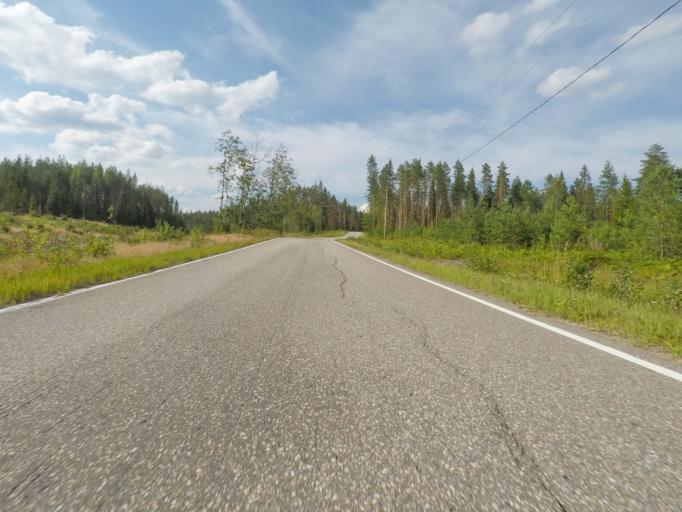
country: FI
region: Southern Savonia
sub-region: Savonlinna
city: Sulkava
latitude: 61.7651
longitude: 28.2371
